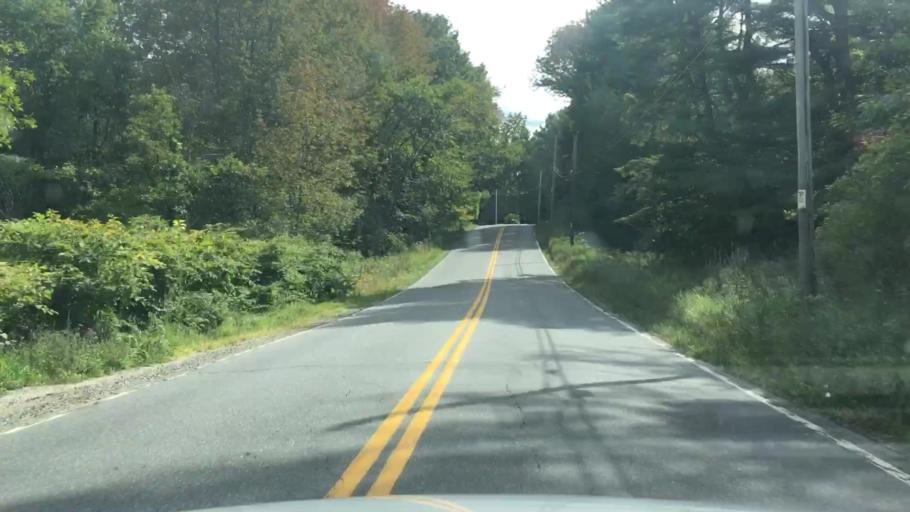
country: US
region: Maine
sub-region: Androscoggin County
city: Lewiston
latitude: 44.0293
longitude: -70.1838
